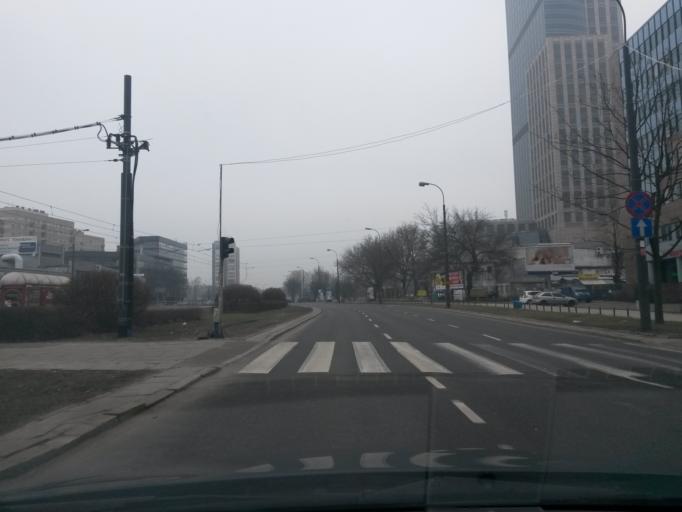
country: PL
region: Masovian Voivodeship
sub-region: Warszawa
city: Wola
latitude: 52.2334
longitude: 20.9823
